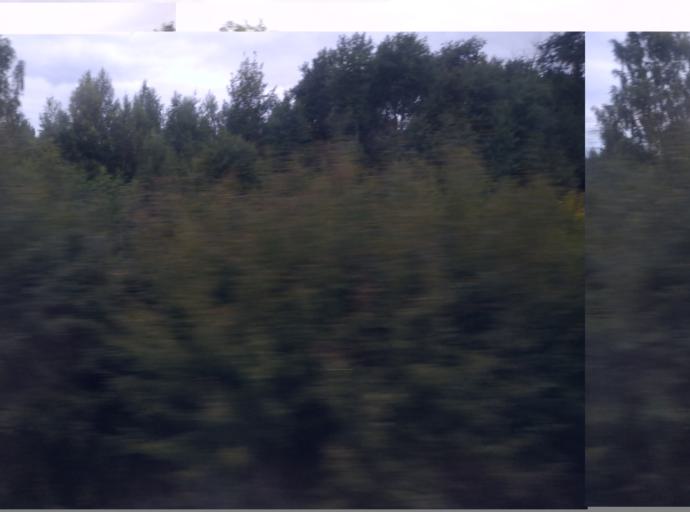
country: RU
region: Kostroma
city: Nerekhta
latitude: 57.4779
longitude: 40.5847
